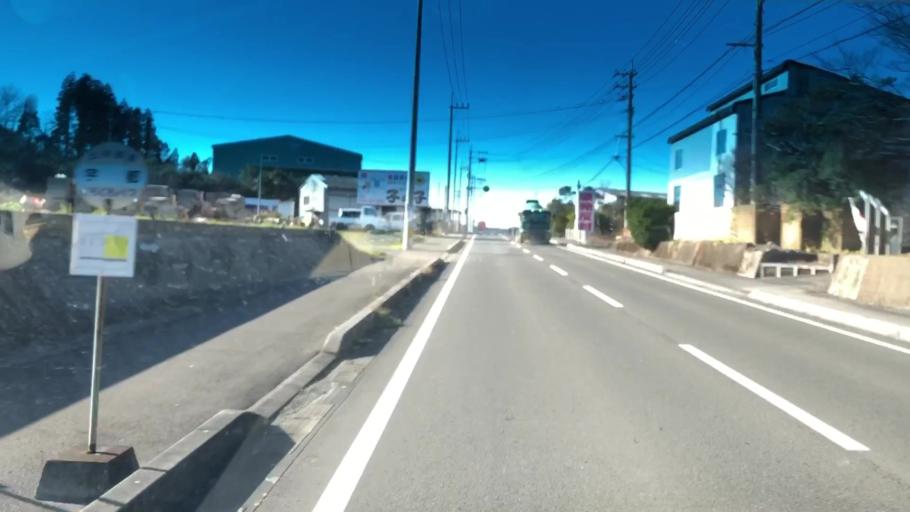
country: JP
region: Kagoshima
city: Satsumasendai
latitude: 31.8202
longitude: 130.2640
